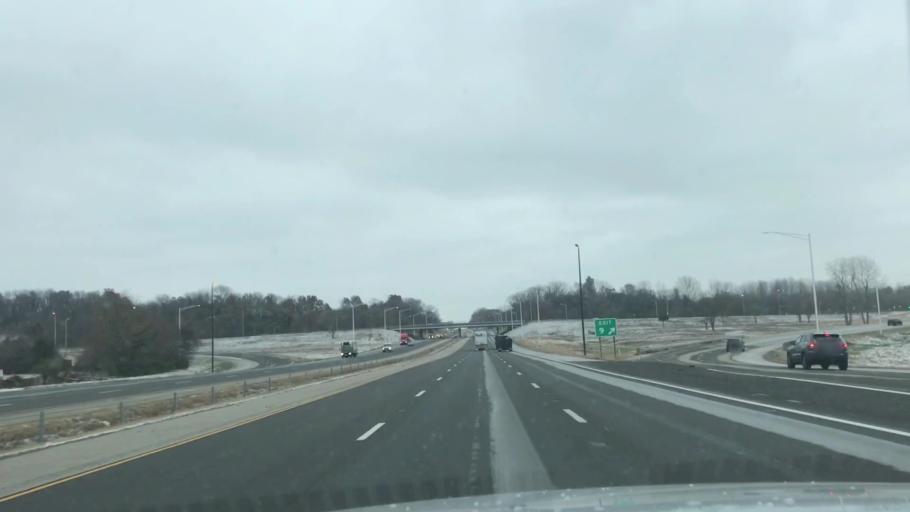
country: US
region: Illinois
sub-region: Madison County
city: Glen Carbon
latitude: 38.7565
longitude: -90.0128
